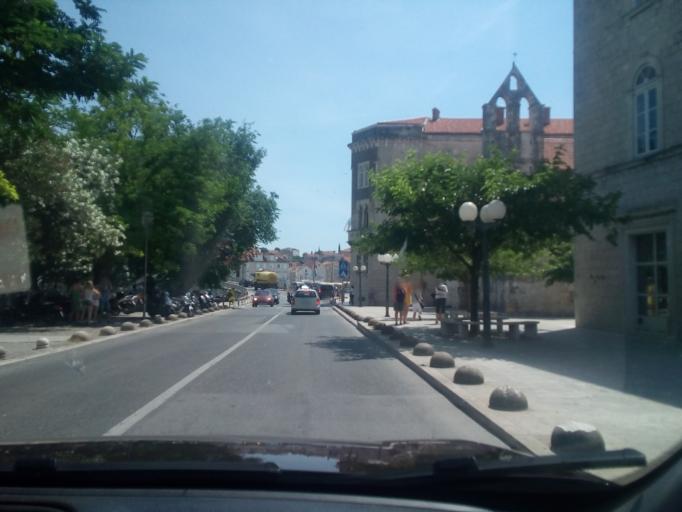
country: HR
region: Splitsko-Dalmatinska
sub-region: Grad Trogir
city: Trogir
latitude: 43.5169
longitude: 16.2519
